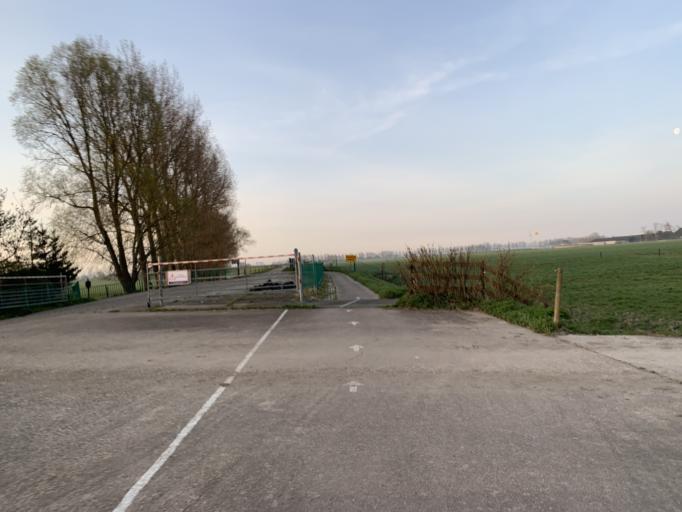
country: NL
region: Groningen
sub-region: Gemeente Winsum
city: Winsum
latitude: 53.2818
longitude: 6.5049
